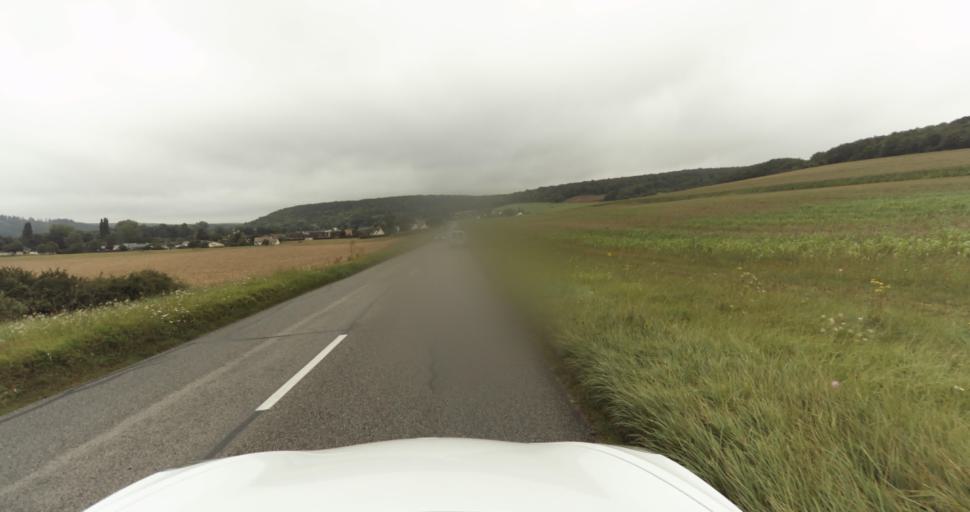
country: FR
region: Haute-Normandie
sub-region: Departement de l'Eure
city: Normanville
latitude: 49.0722
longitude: 1.1694
